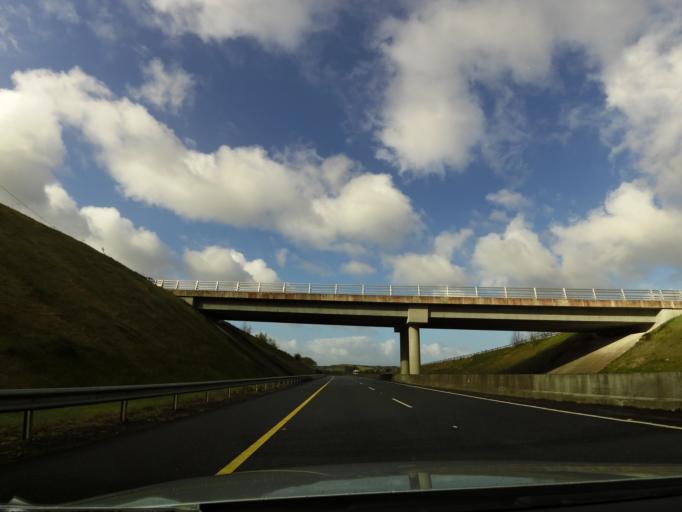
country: IE
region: Munster
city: Ballina
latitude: 52.7833
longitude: -8.3690
